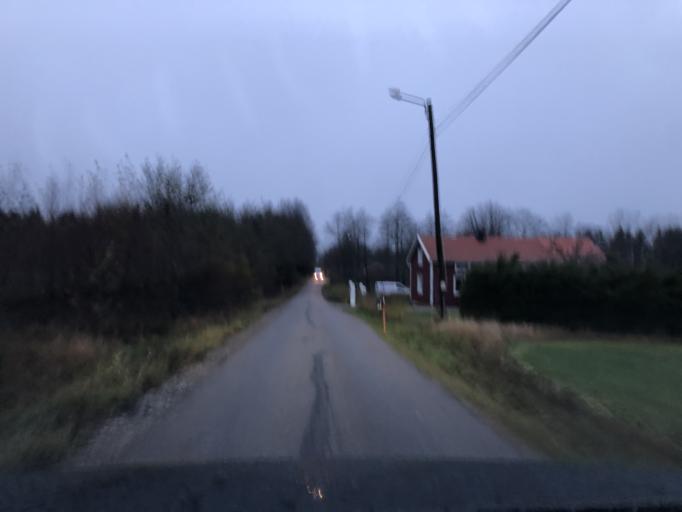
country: SE
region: Vaestra Goetaland
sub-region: Boras Kommun
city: Sjomarken
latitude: 57.7647
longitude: 12.8492
